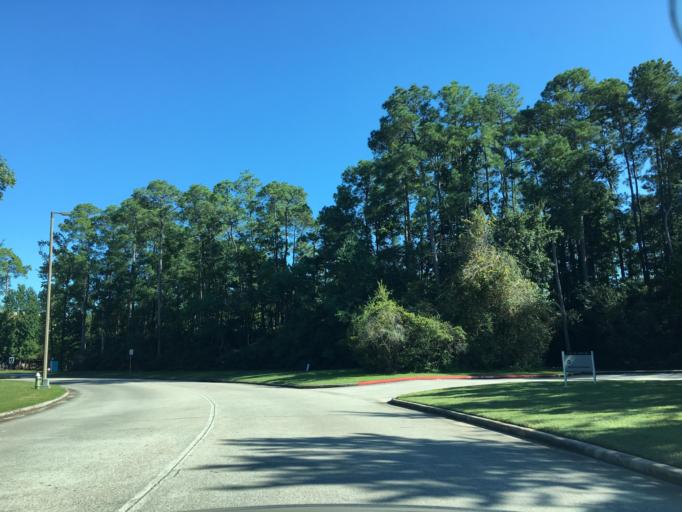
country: US
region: Texas
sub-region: Montgomery County
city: Shenandoah
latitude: 30.2052
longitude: -95.4607
